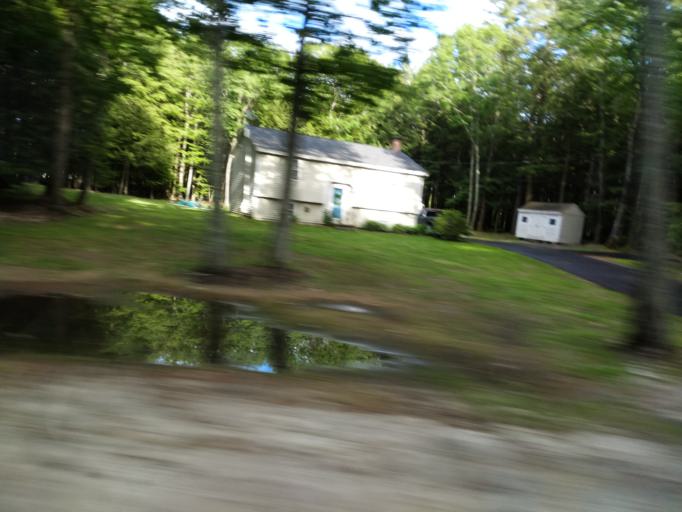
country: US
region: Maine
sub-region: Cumberland County
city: New Gloucester
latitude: 43.8855
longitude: -70.2961
